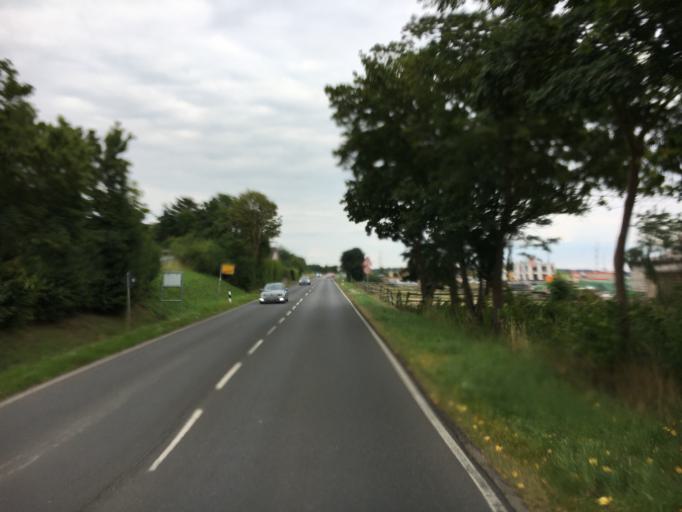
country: DE
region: Hesse
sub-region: Regierungsbezirk Giessen
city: Kirchhain
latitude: 50.8248
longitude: 8.9416
